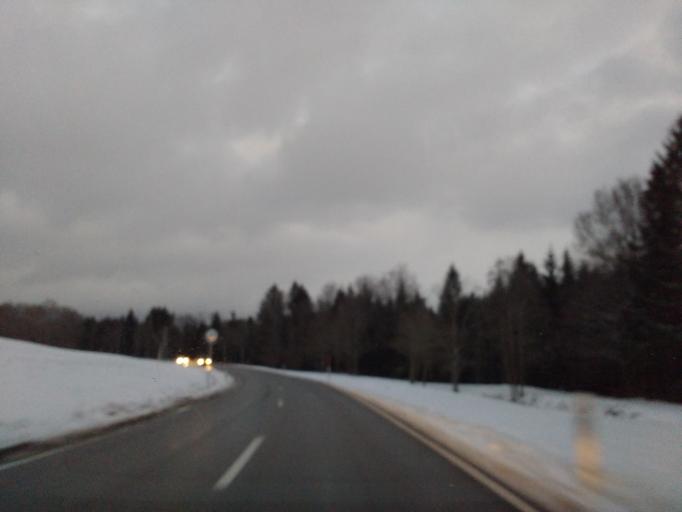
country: DE
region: Bavaria
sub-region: Swabia
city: Buchenberg
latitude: 47.7161
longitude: 10.2335
